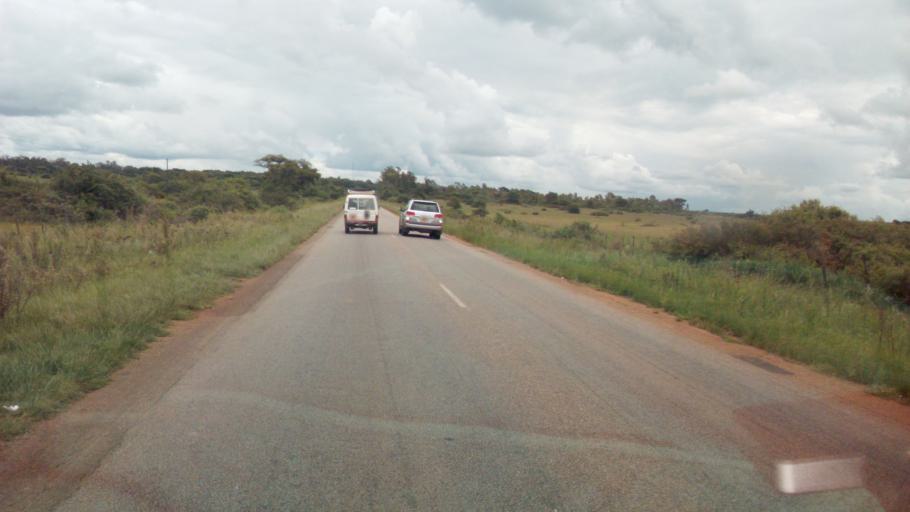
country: ZW
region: Harare
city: Harare
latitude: -17.7196
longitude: 31.0175
